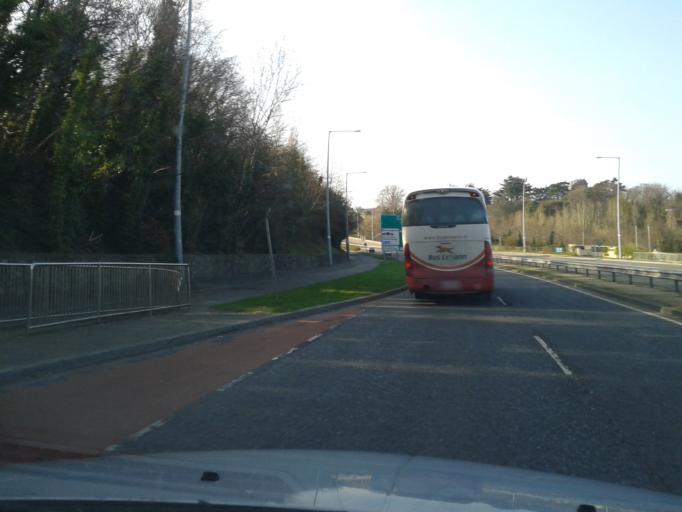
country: IE
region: Leinster
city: Loughlinstown
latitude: 53.2426
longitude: -6.1305
